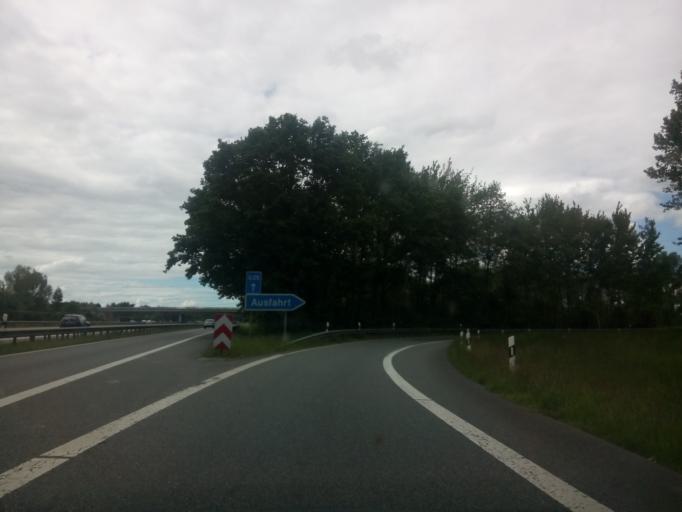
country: DE
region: Lower Saxony
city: Ritterhude
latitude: 53.1447
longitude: 8.7362
